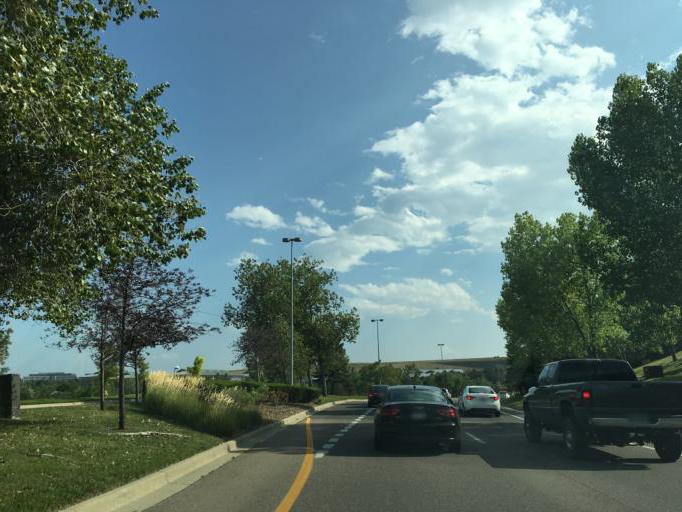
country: US
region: Colorado
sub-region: Broomfield County
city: Broomfield
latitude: 39.9252
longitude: -105.1279
